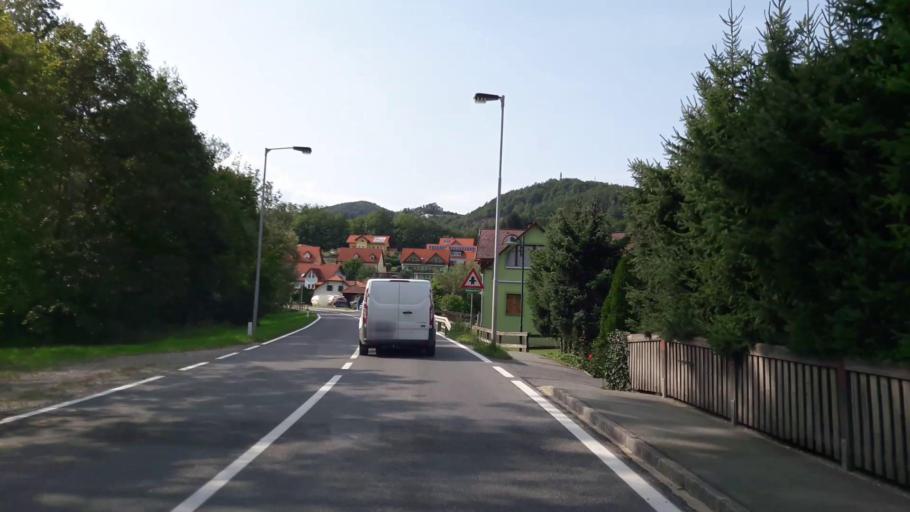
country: AT
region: Styria
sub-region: Politischer Bezirk Hartberg-Fuerstenfeld
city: Stubenberg
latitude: 47.2390
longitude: 15.7965
